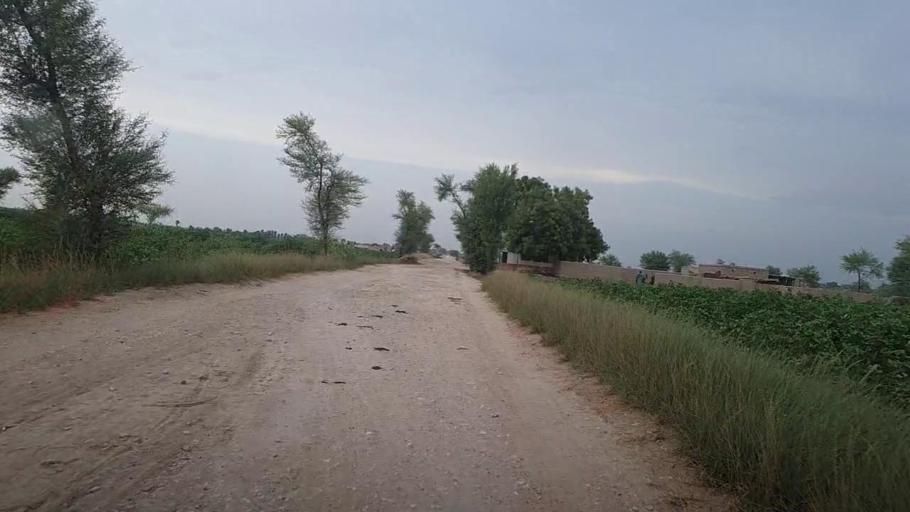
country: PK
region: Sindh
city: Karaundi
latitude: 26.9660
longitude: 68.3438
